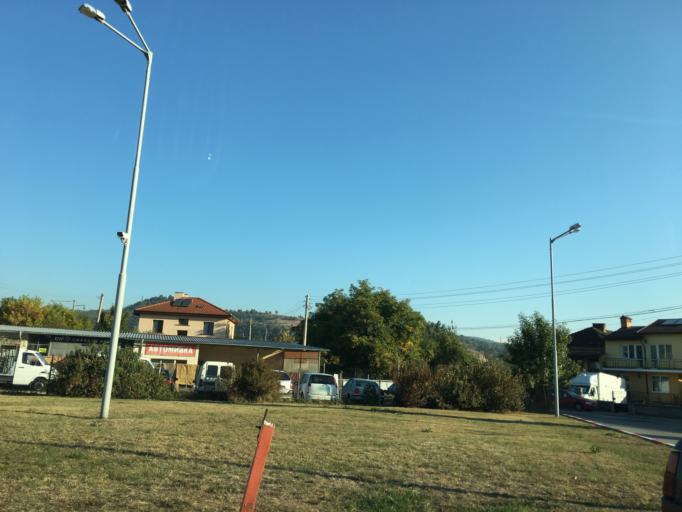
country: BG
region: Sofiya
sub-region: Obshtina Dolna Banya
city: Dolna Banya
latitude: 42.3144
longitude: 23.8572
